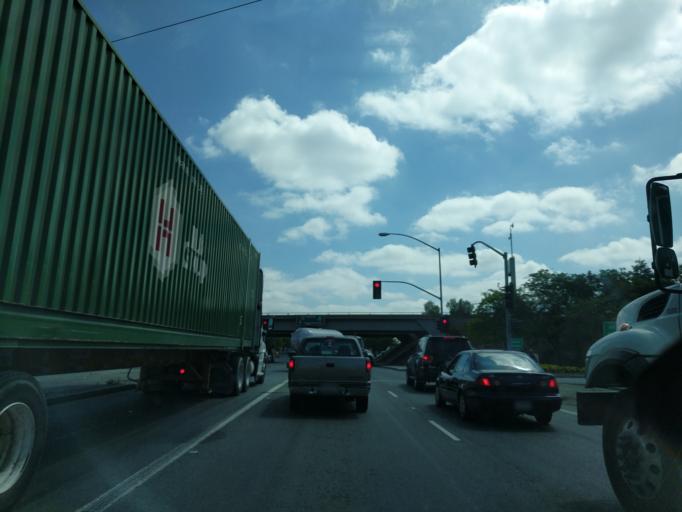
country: US
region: California
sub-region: San Joaquin County
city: Stockton
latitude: 37.9365
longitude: -121.2987
